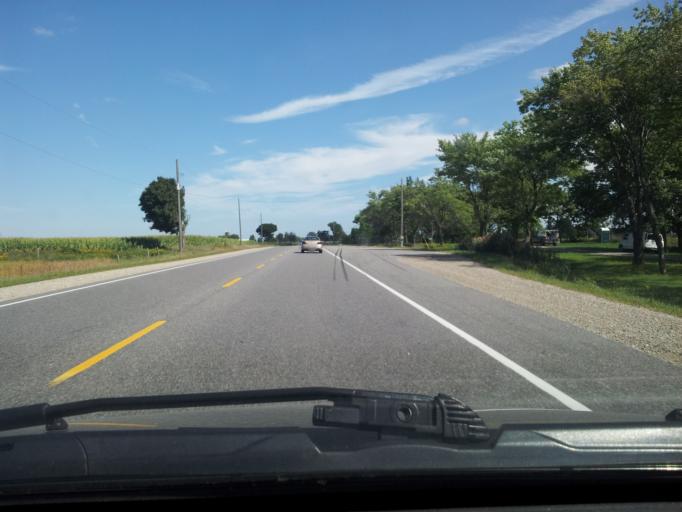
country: CA
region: Ontario
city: Stratford
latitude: 43.3690
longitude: -80.7726
